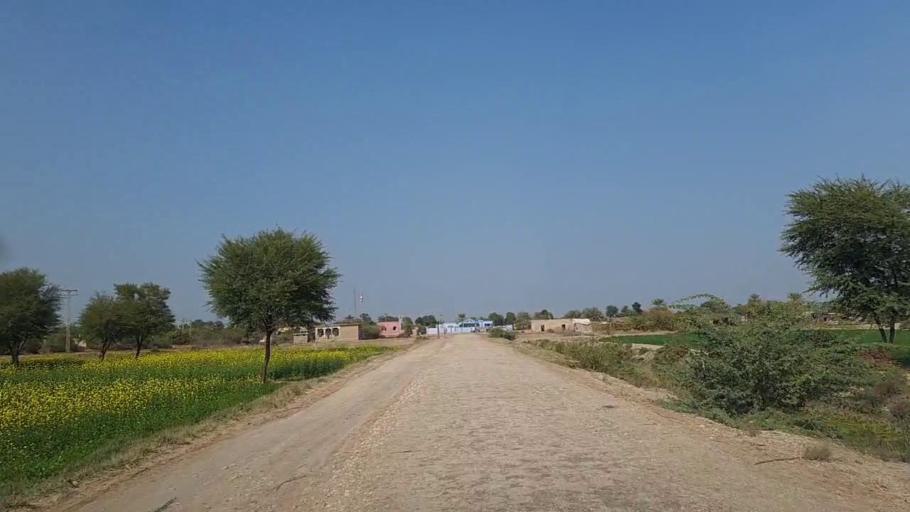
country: PK
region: Sindh
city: Jam Sahib
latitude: 26.2740
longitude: 68.5289
